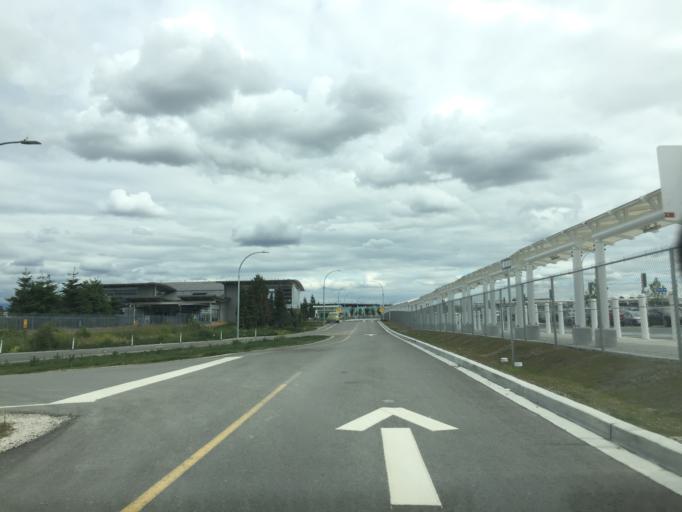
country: CA
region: British Columbia
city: Richmond
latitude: 49.1961
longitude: -123.1483
